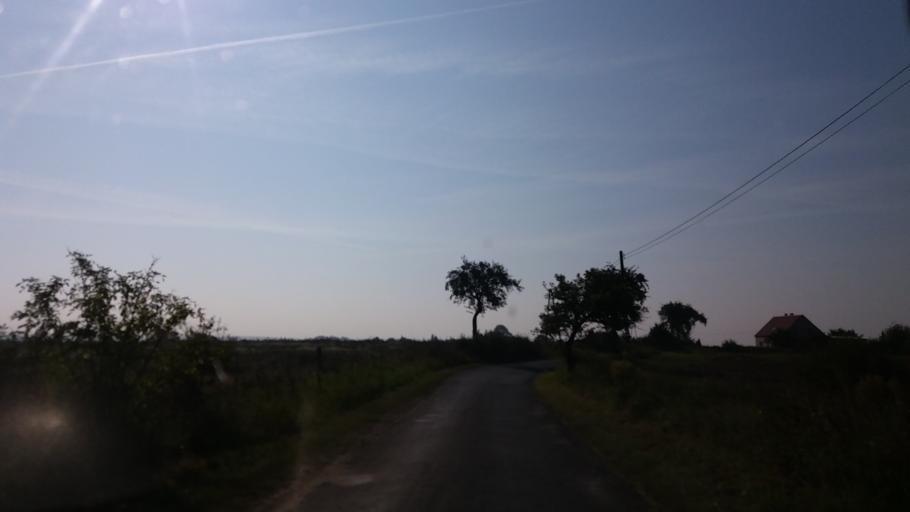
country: PL
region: West Pomeranian Voivodeship
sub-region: Powiat choszczenski
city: Pelczyce
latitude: 53.0238
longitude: 15.3272
